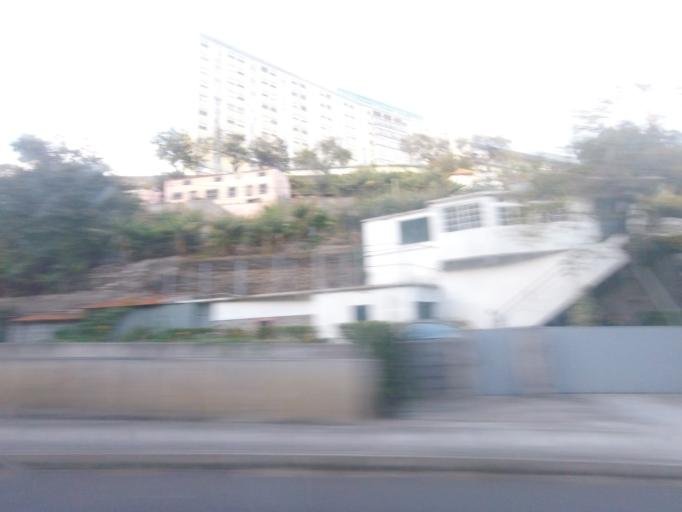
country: PT
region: Madeira
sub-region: Funchal
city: Funchal
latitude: 32.6475
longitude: -16.9248
